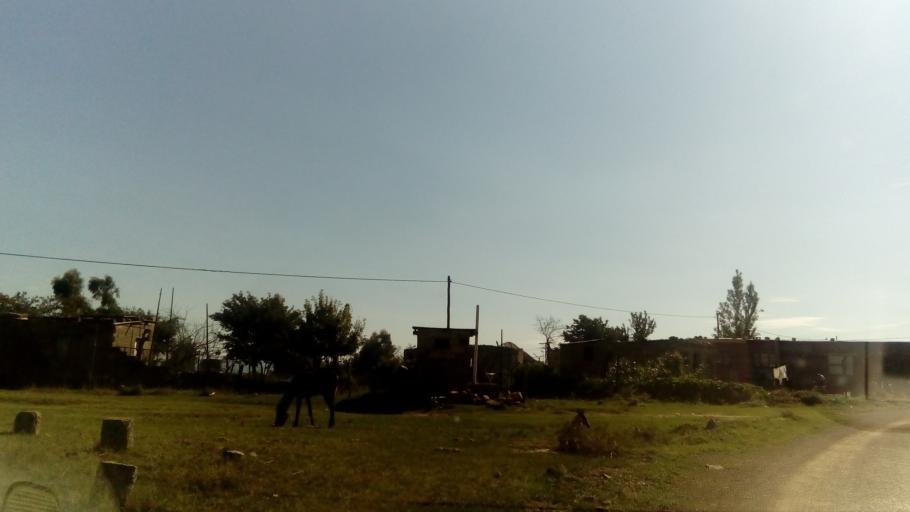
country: LS
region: Berea
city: Teyateyaneng
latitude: -29.1378
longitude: 27.7493
